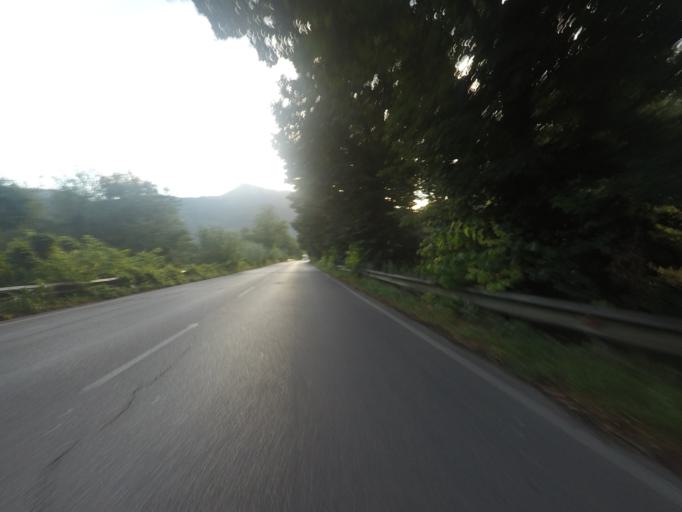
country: IT
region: Tuscany
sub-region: Provincia di Lucca
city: Corsanico-Bargecchia
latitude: 43.9373
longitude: 10.2917
